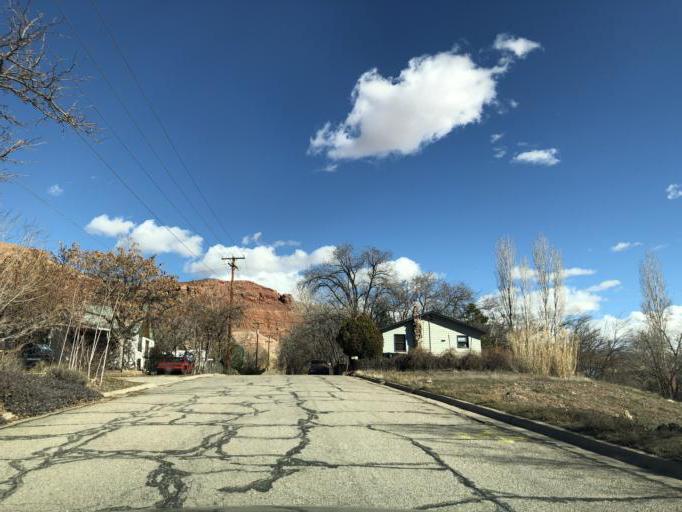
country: US
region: Utah
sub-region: Grand County
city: Moab
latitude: 38.5778
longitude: -109.5494
